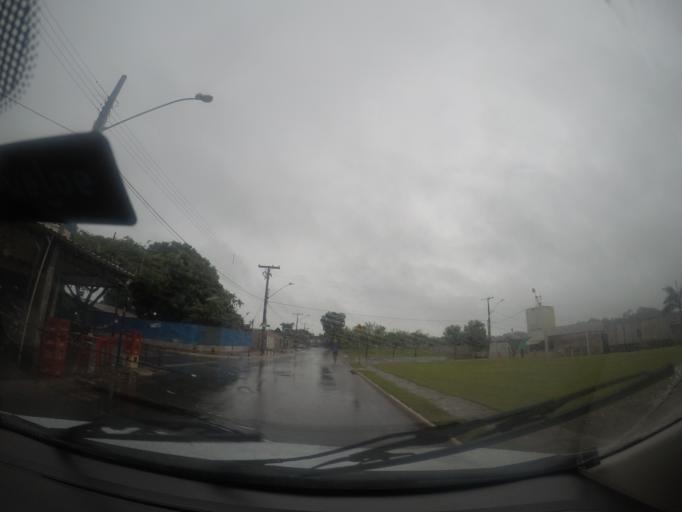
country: BR
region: Goias
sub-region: Goiania
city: Goiania
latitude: -16.6065
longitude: -49.3478
